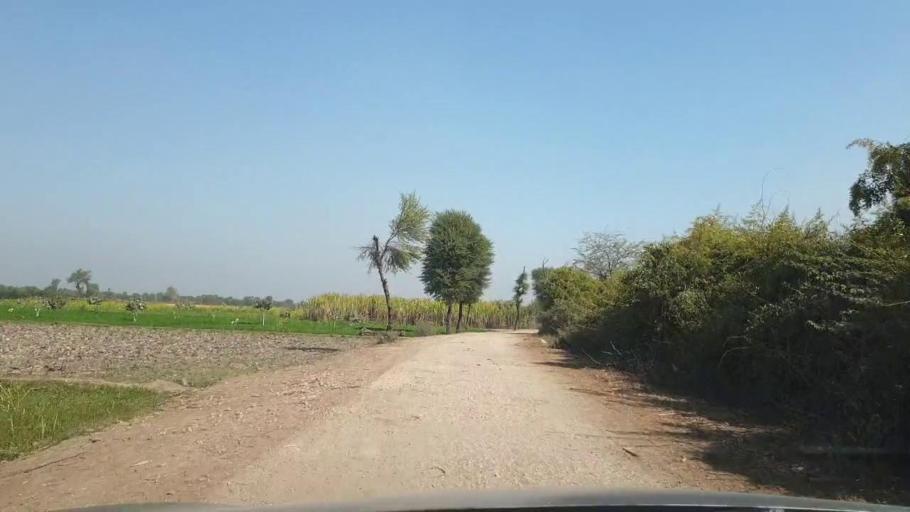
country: PK
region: Sindh
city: Tando Allahyar
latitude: 25.5844
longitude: 68.6499
